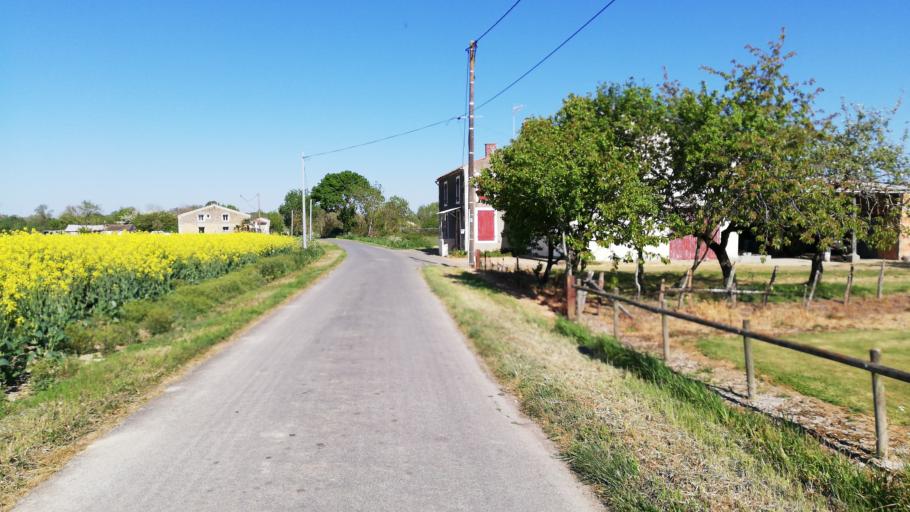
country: FR
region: Pays de la Loire
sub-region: Departement de la Vendee
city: Maillezais
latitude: 46.3267
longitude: -0.7468
